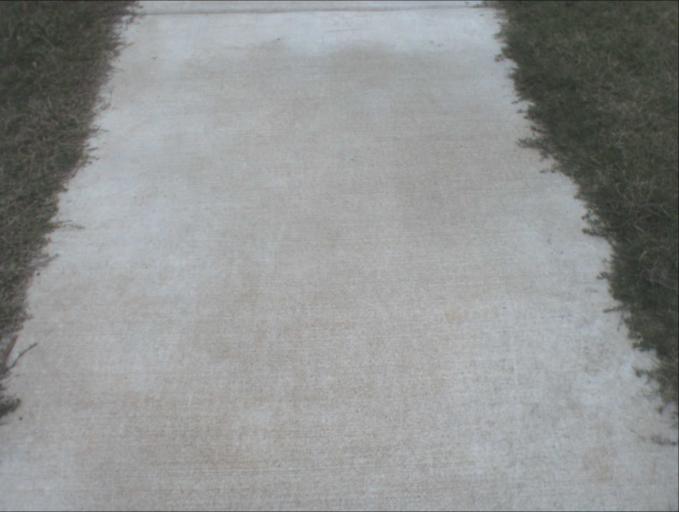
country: AU
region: Queensland
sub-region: Logan
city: Chambers Flat
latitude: -27.7976
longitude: 153.1078
